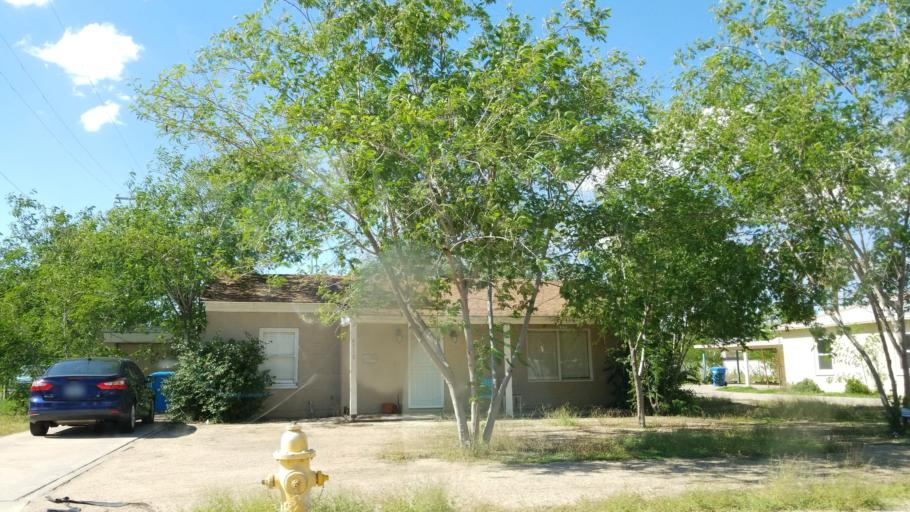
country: US
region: Arizona
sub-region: Maricopa County
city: Phoenix
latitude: 33.5067
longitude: -112.0782
